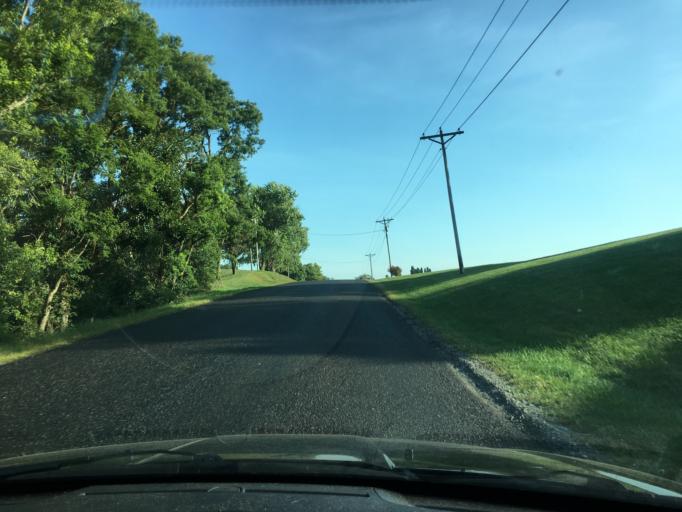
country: US
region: Ohio
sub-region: Logan County
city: West Liberty
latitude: 40.2920
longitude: -83.7296
